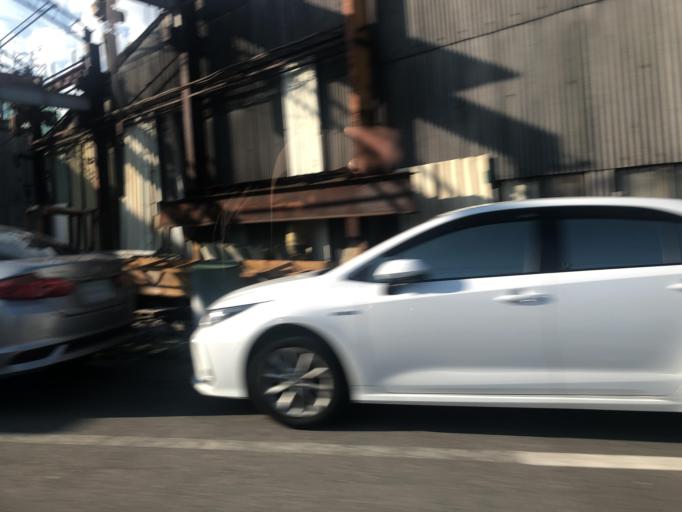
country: TW
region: Taiwan
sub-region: Tainan
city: Tainan
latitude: 23.0304
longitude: 120.1933
